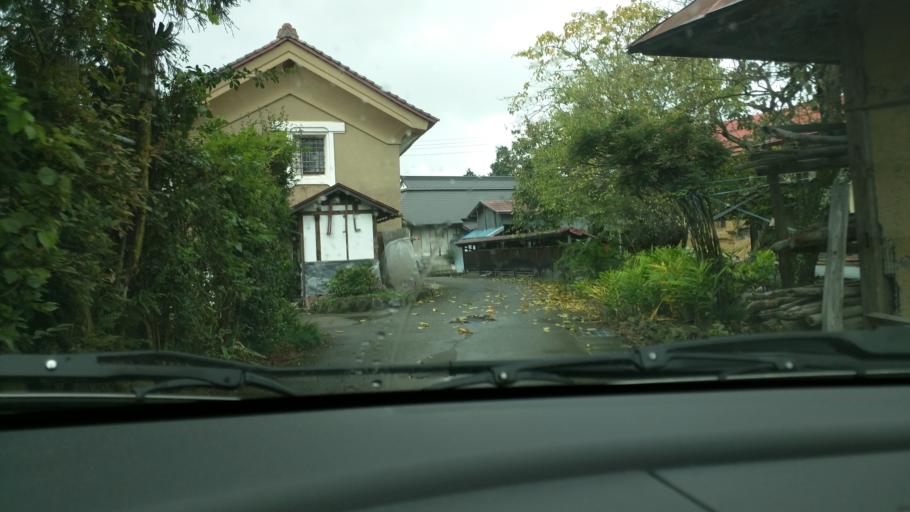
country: JP
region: Fukushima
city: Kitakata
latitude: 37.4625
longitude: 139.8581
